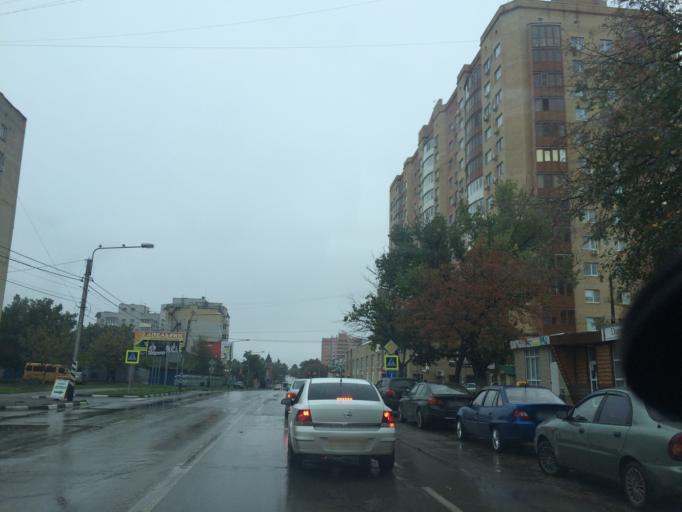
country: RU
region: Rostov
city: Azov
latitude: 47.1078
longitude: 39.4296
